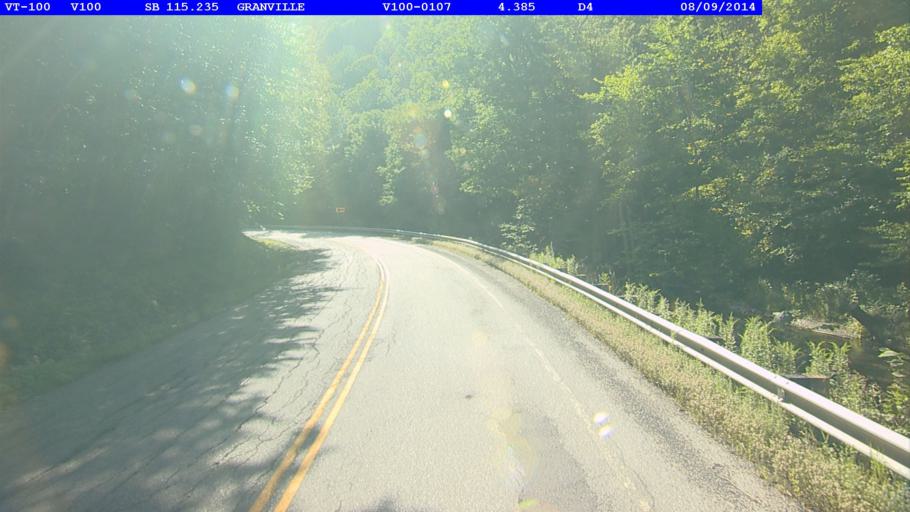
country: US
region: Vermont
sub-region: Orange County
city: Randolph
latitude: 44.0036
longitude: -72.8518
